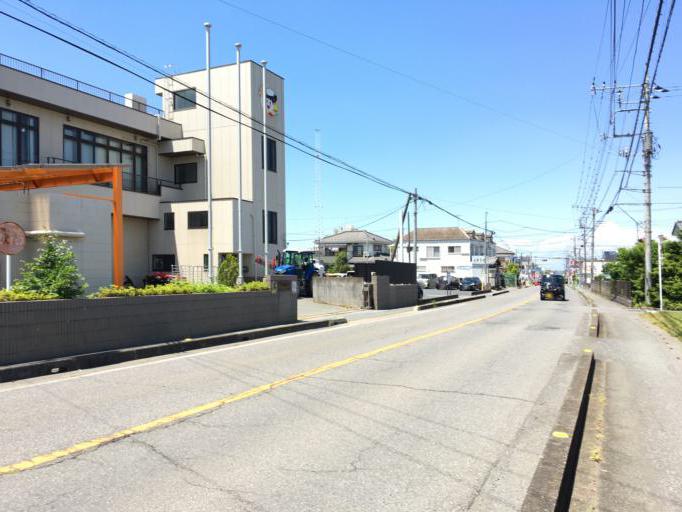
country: JP
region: Saitama
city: Sakado
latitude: 35.9472
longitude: 139.3874
